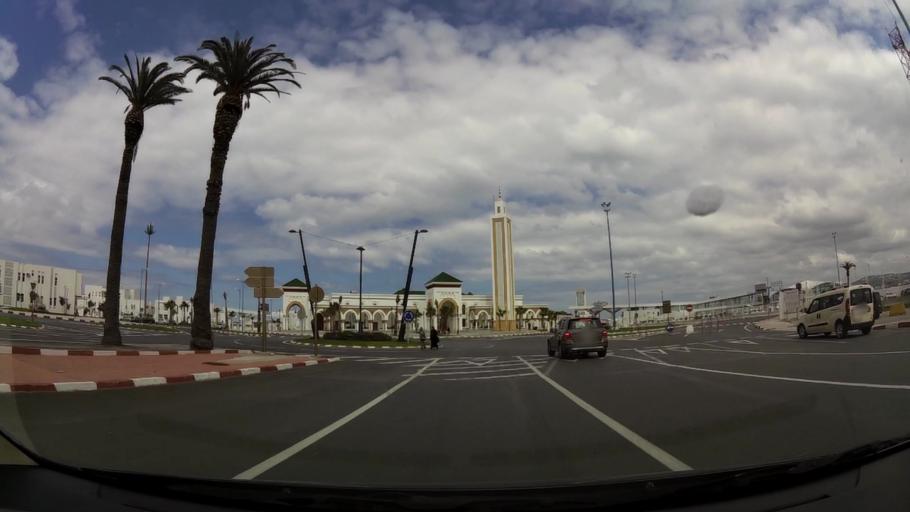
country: MA
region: Tanger-Tetouan
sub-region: Tanger-Assilah
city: Tangier
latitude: 35.7884
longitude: -5.8076
